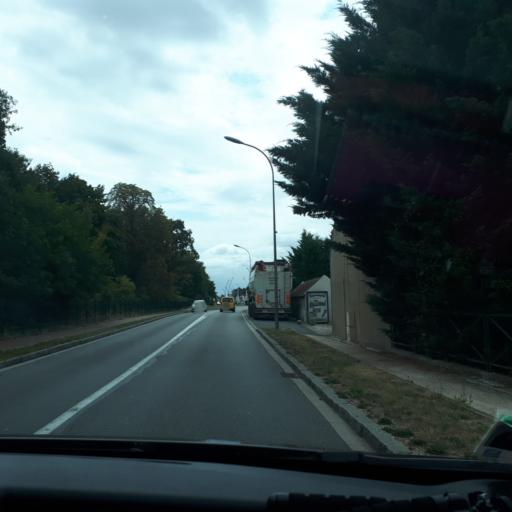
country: FR
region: Centre
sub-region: Departement du Loiret
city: Saint-Pere-sur-Loire
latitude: 47.7946
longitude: 2.3811
